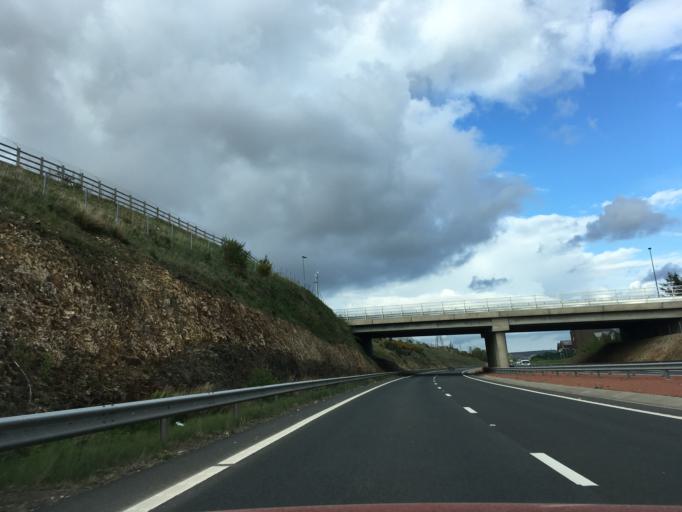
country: GB
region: Wales
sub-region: Blaenau Gwent
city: Tredegar
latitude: 51.7979
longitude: -3.2412
